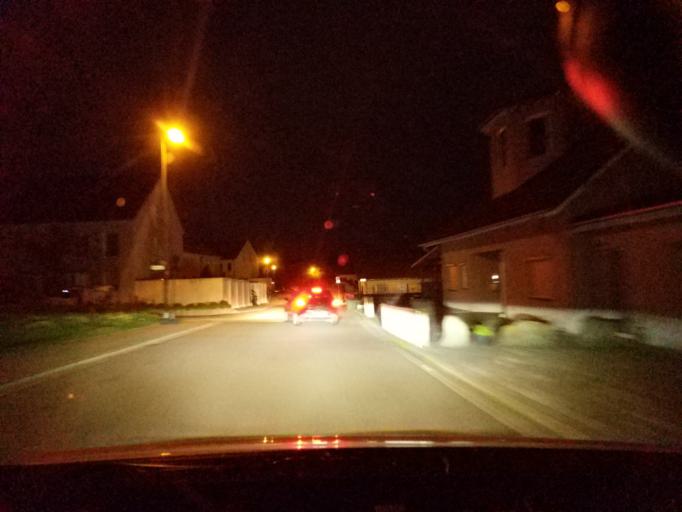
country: DE
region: Rheinland-Pfalz
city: Otterbach
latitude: 49.4905
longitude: 7.7249
